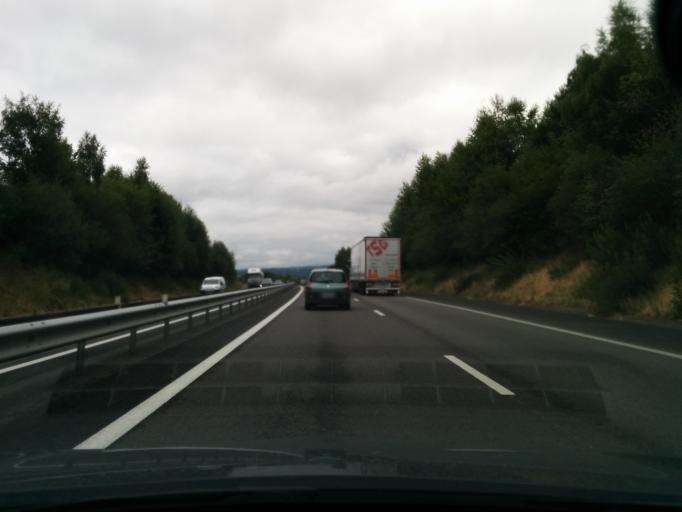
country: FR
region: Limousin
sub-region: Departement de la Correze
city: Sainte-Fereole
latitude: 45.2845
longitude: 1.5692
